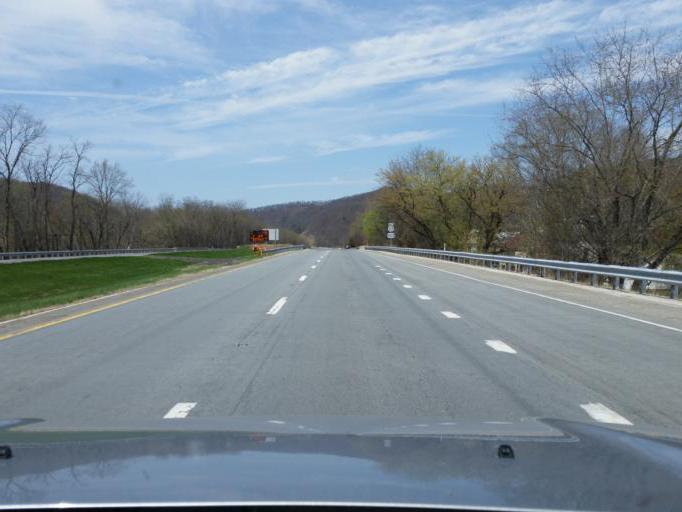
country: US
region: Pennsylvania
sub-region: Perry County
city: Newport
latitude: 40.5476
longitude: -77.1549
